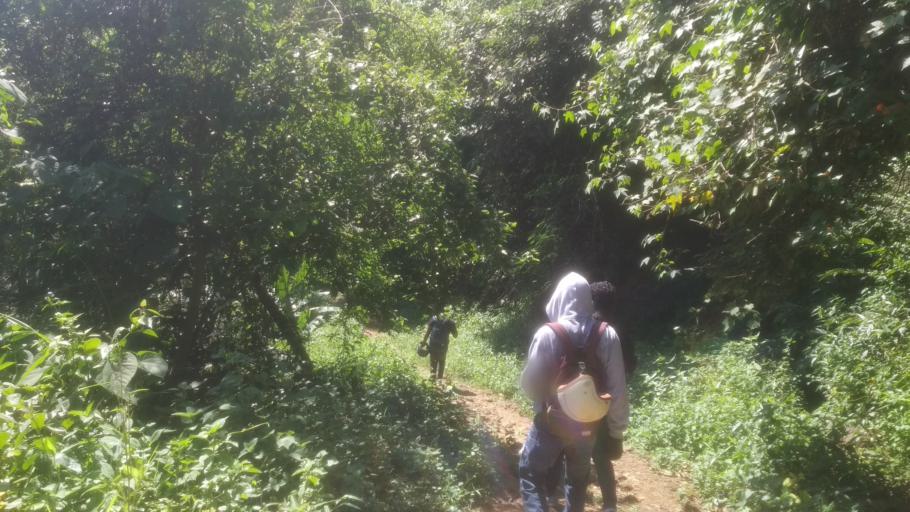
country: IN
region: Kerala
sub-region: Idukki
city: Idukki
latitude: 9.9768
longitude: 76.8370
